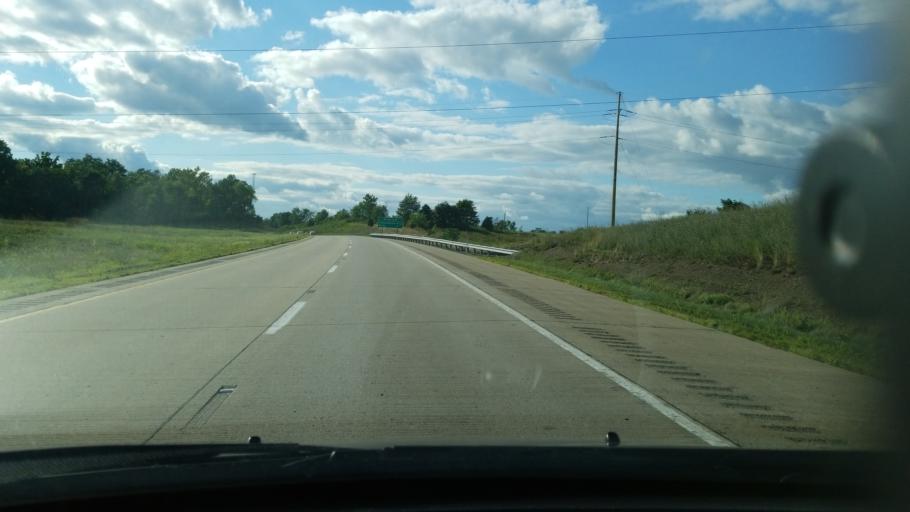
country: US
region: Pennsylvania
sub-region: Northumberland County
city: Milton
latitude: 41.0004
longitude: -76.7490
